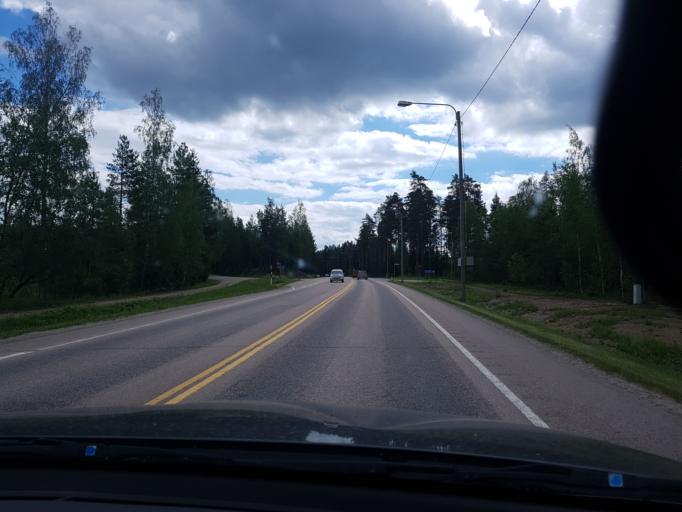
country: FI
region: Pirkanmaa
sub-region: Tampere
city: Paelkaene
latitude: 61.3178
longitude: 24.2846
